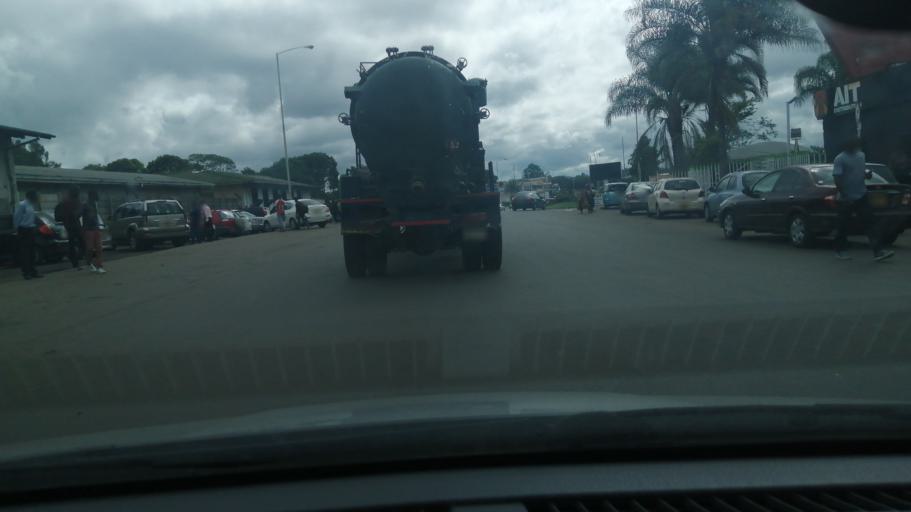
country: ZW
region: Harare
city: Harare
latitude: -17.8301
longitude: 31.0586
